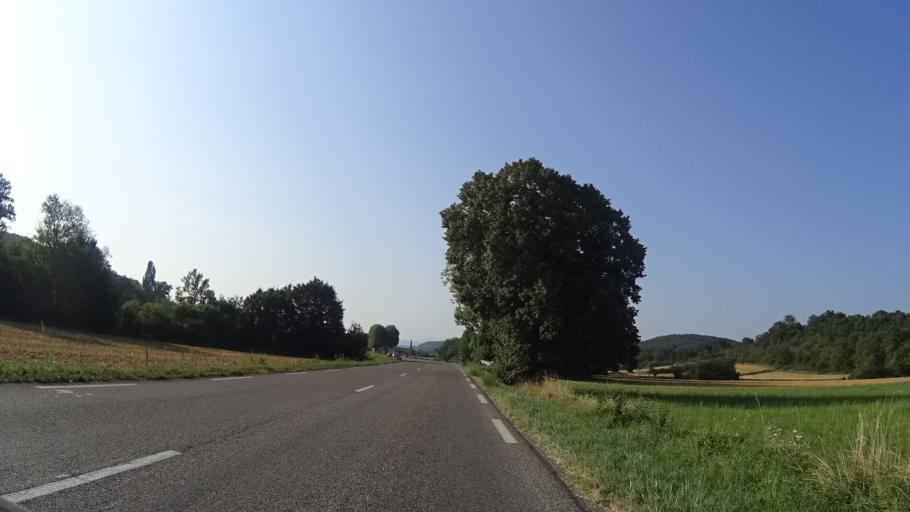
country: FR
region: Midi-Pyrenees
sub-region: Departement de l'Ariege
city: Mirepoix
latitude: 43.0611
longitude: 1.8820
